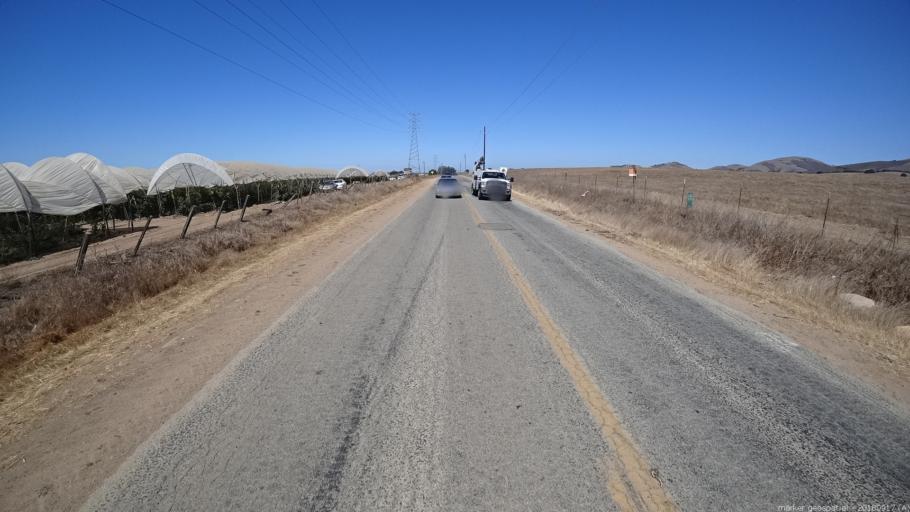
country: US
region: California
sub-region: Monterey County
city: Salinas
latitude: 36.7137
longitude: -121.5882
